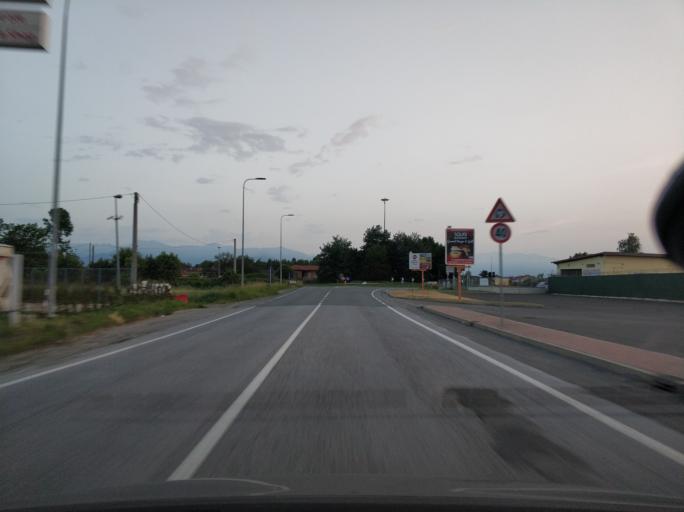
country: IT
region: Piedmont
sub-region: Provincia di Torino
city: San Maurizio
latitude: 45.2042
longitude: 7.6367
